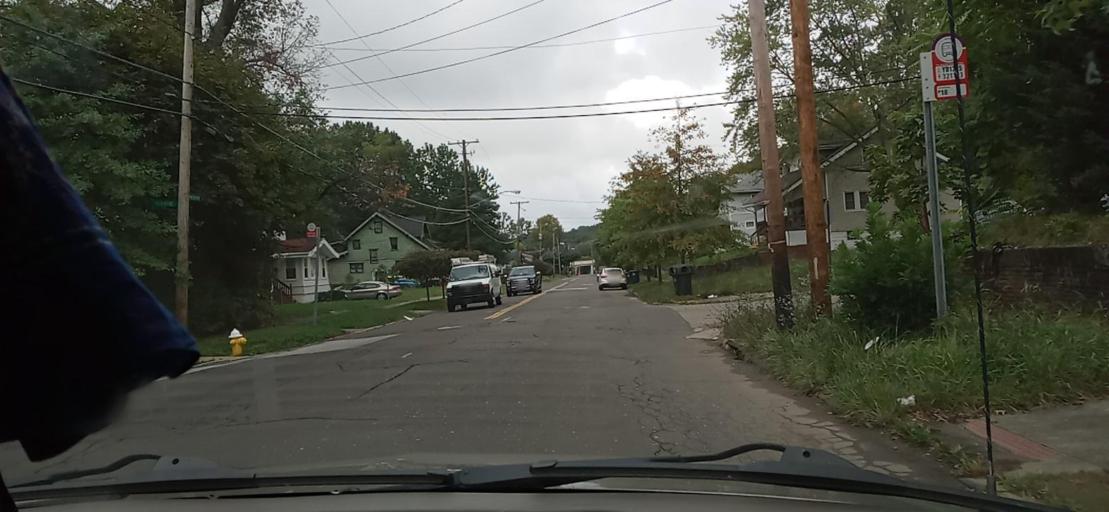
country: US
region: Ohio
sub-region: Summit County
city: Akron
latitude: 41.0651
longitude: -81.5503
